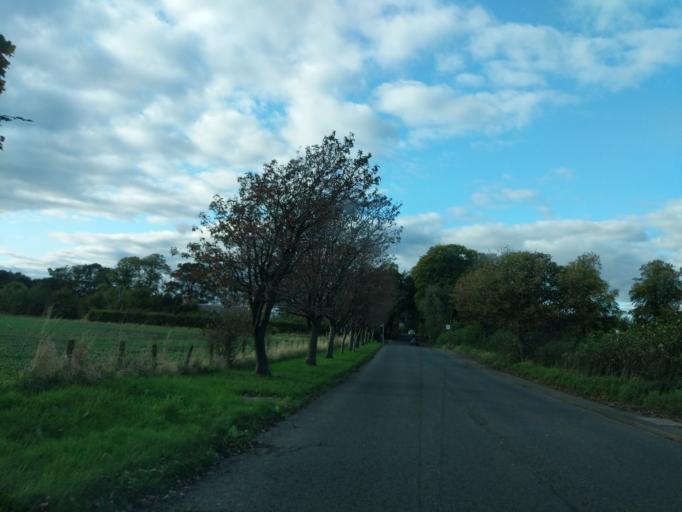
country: GB
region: Scotland
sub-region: Edinburgh
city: Queensferry
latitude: 55.9857
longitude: -3.3757
